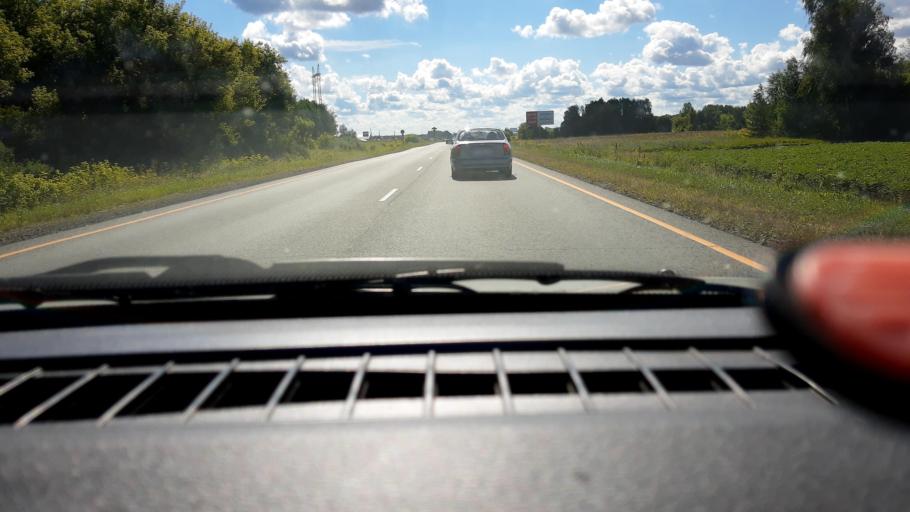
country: RU
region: Nizjnij Novgorod
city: Arzamas
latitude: 55.3137
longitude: 43.8978
